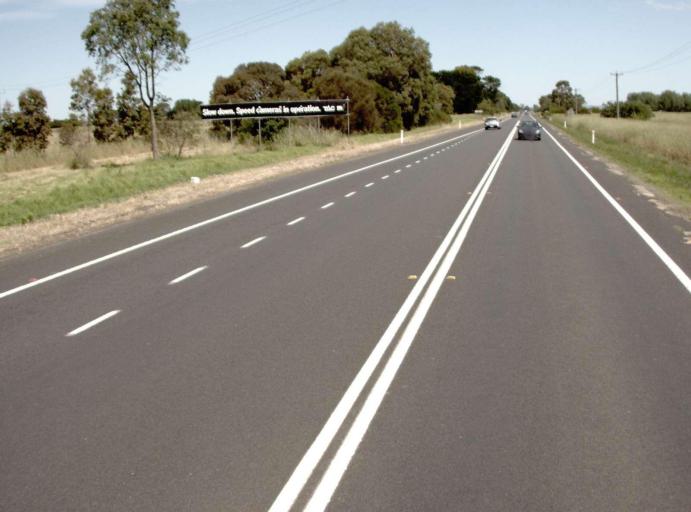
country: AU
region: Victoria
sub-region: Wellington
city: Sale
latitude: -38.0466
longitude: 147.0642
